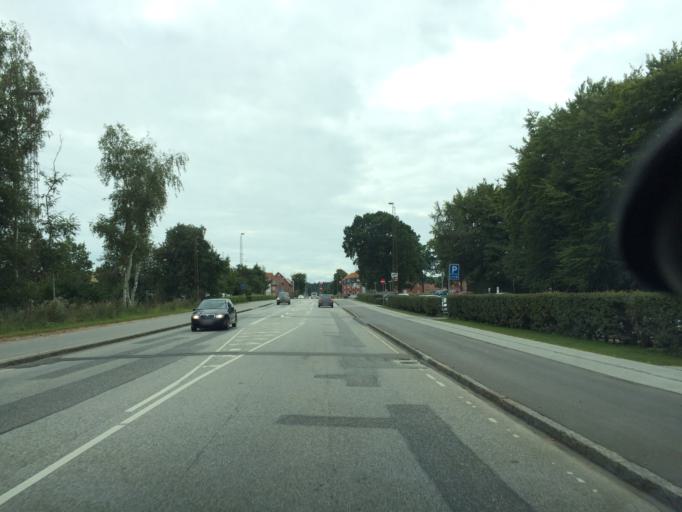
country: DK
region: South Denmark
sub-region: Aabenraa Kommune
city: Aabenraa
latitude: 55.0362
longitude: 9.4071
